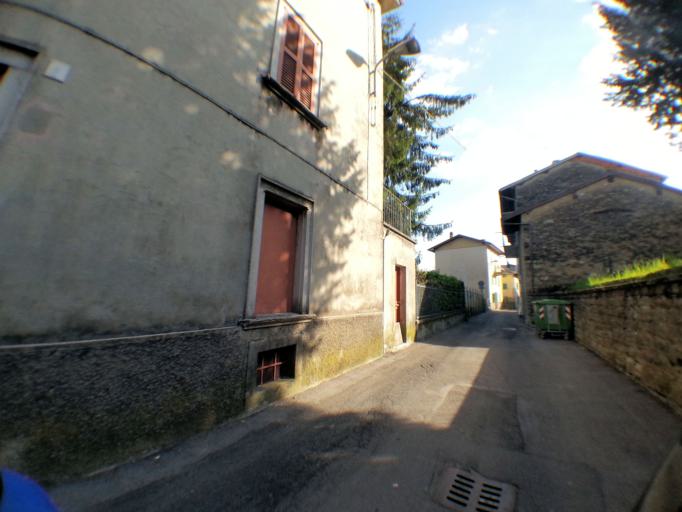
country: IT
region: Lombardy
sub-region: Provincia di Como
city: Pigra
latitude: 45.9583
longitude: 9.1285
